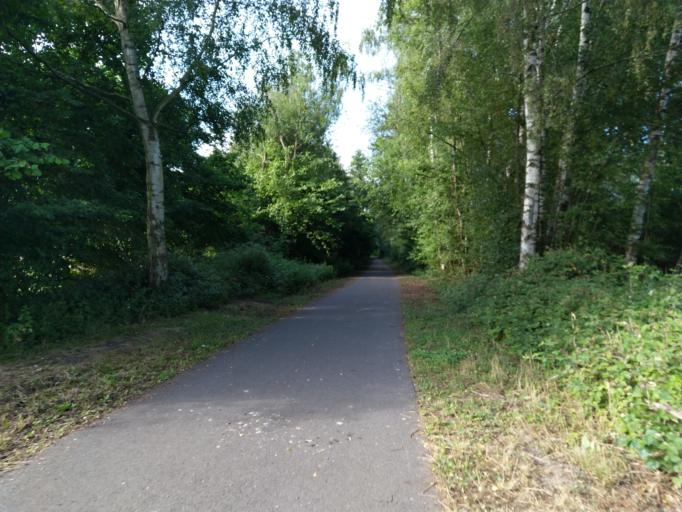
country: BE
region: Wallonia
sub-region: Province du Hainaut
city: Erquelinnes
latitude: 50.3363
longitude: 4.1002
